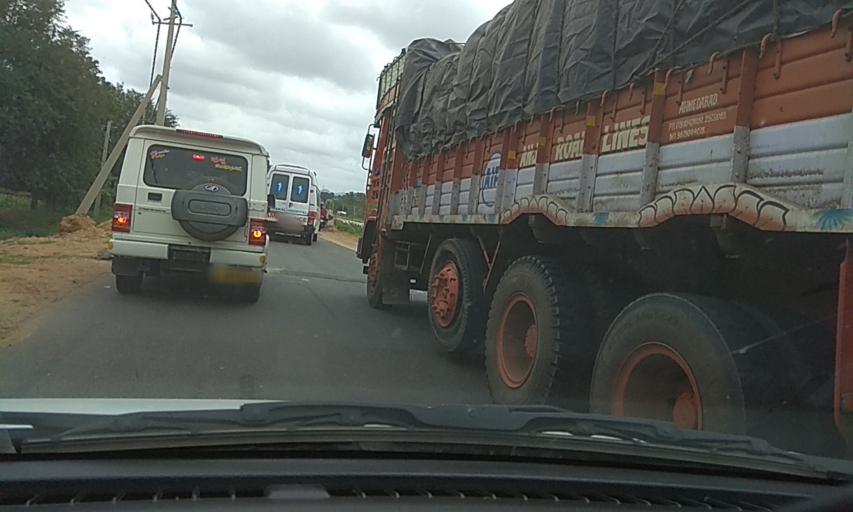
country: IN
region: Karnataka
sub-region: Chitradurga
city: Chitradurga
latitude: 14.2924
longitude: 76.2834
